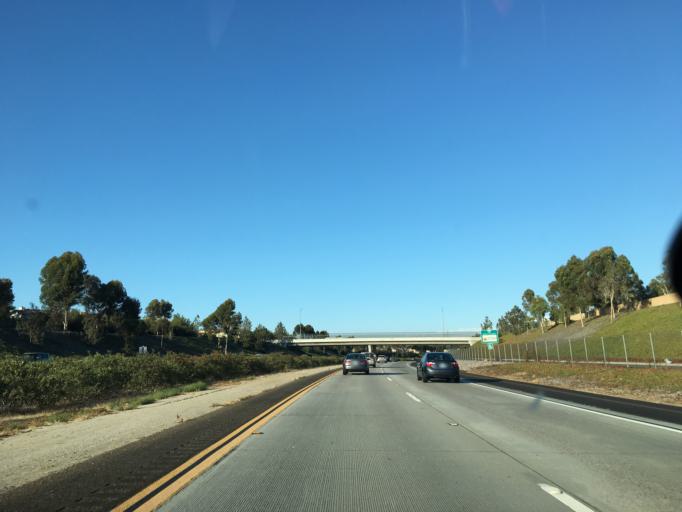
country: US
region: California
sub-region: San Diego County
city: Fairbanks Ranch
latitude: 32.9648
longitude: -117.1795
